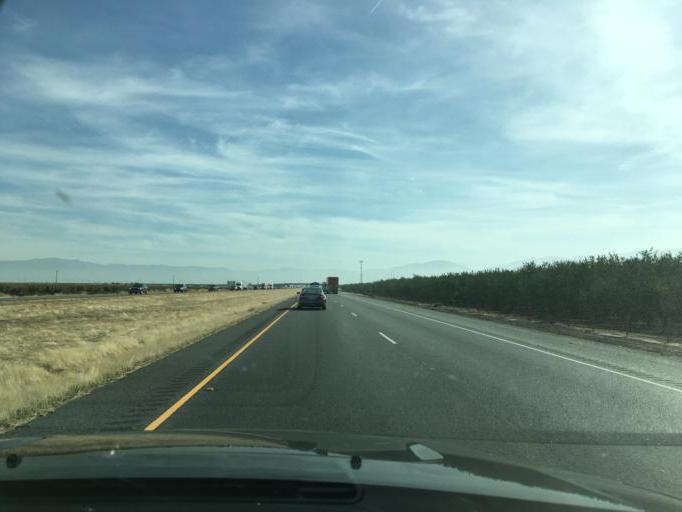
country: US
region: California
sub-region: Kern County
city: Greenfield
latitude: 35.0828
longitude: -119.0248
